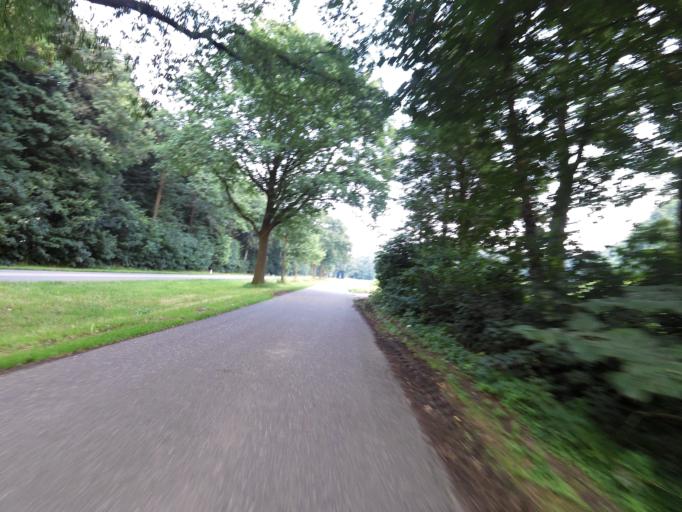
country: NL
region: Gelderland
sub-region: Gemeente Doetinchem
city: Doetinchem
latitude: 51.9935
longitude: 6.2378
